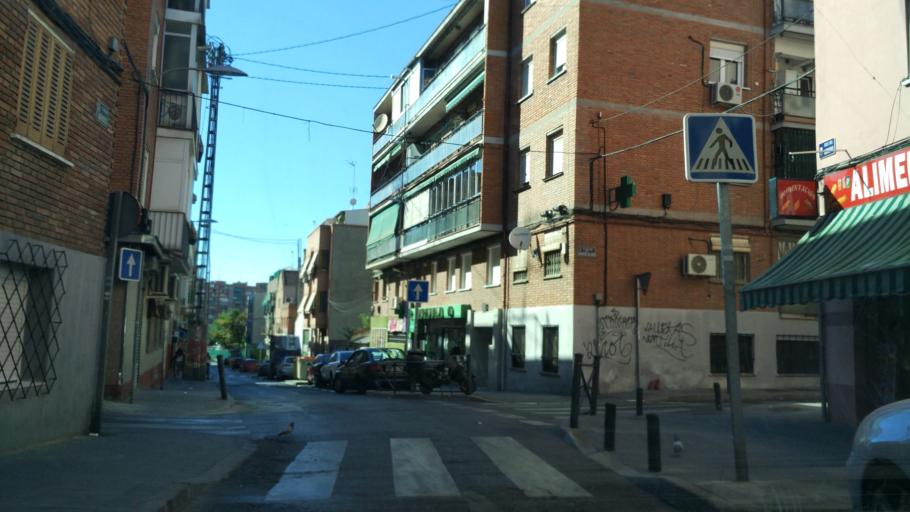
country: ES
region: Madrid
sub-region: Provincia de Madrid
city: Tetuan de las Victorias
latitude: 40.4689
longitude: -3.7010
